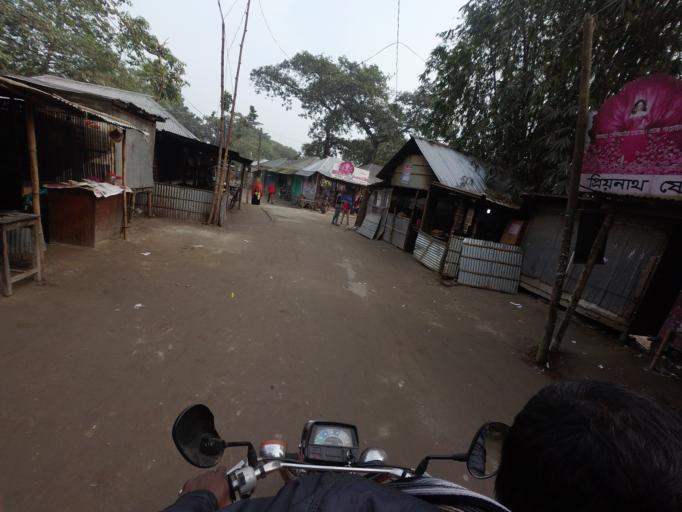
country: BD
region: Rajshahi
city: Saidpur
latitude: 25.9513
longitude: 88.9048
